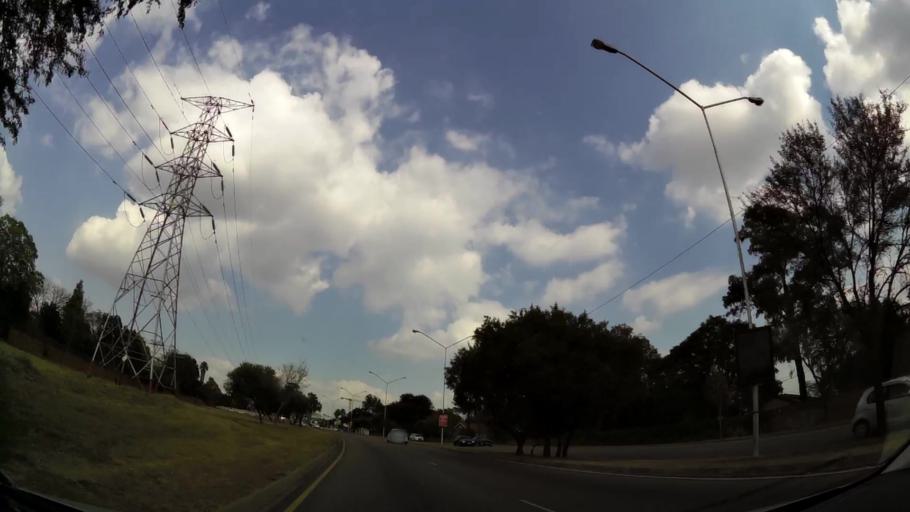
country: ZA
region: Gauteng
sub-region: City of Tshwane Metropolitan Municipality
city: Pretoria
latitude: -25.7811
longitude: 28.2870
